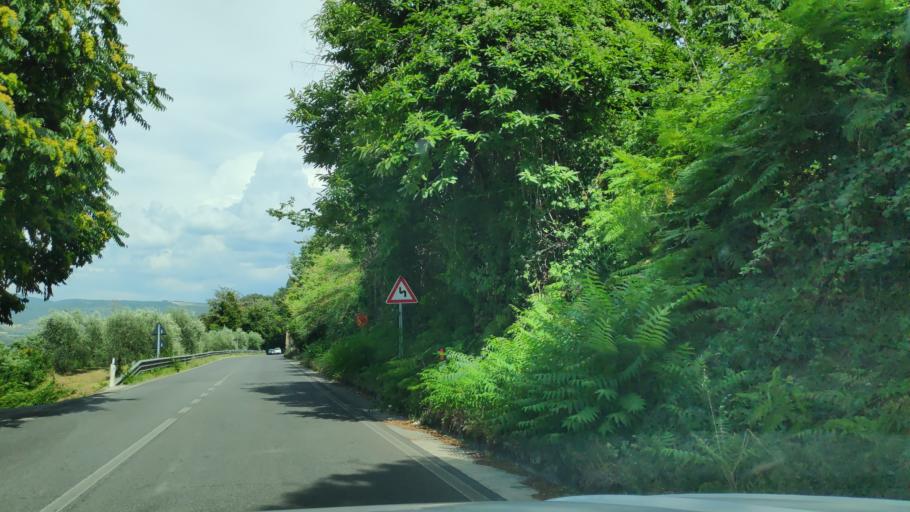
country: IT
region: Umbria
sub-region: Provincia di Terni
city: Orvieto
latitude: 42.7222
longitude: 12.1051
